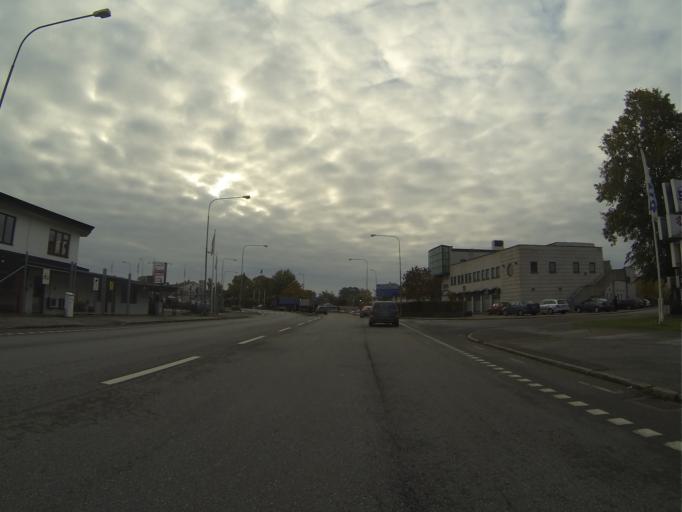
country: SE
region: Skane
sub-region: Tomelilla Kommun
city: Tomelilla
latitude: 55.5476
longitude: 13.9451
